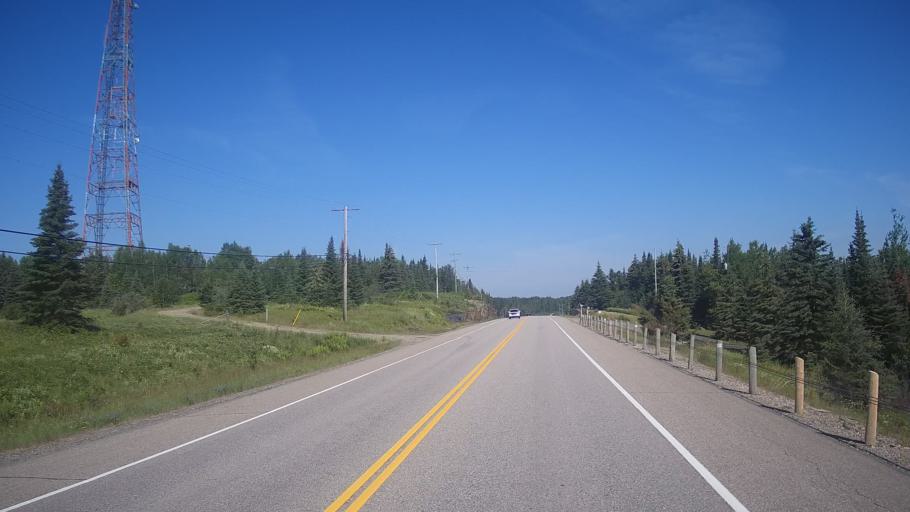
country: CA
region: Ontario
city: Dryden
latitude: 49.7647
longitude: -92.6801
